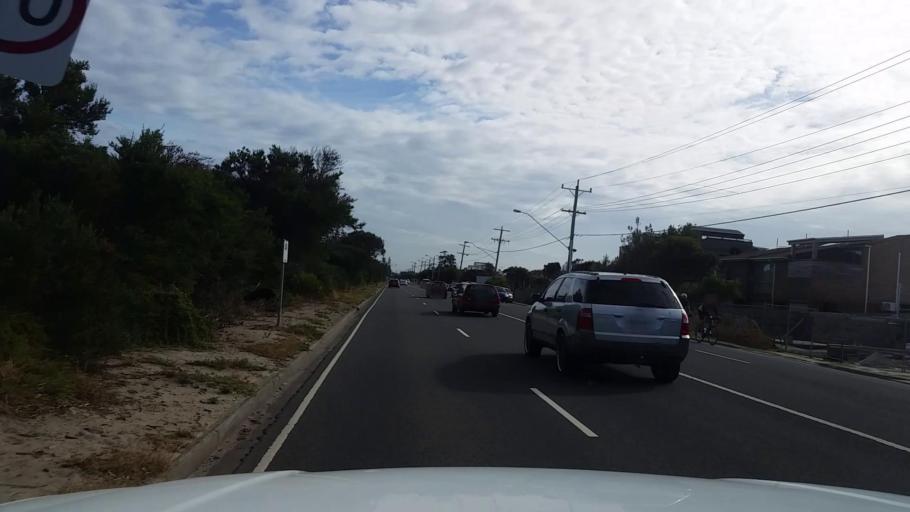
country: AU
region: Victoria
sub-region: Frankston
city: Seaford
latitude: -38.0979
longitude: 145.1257
